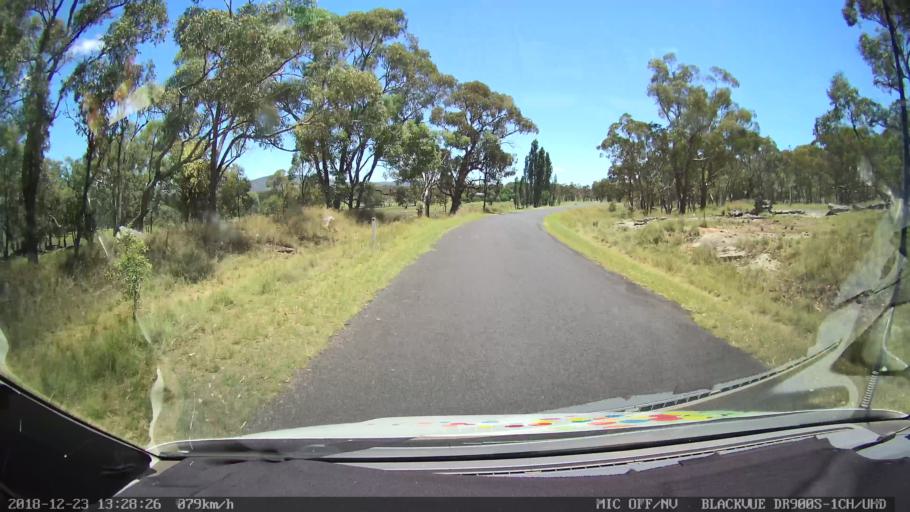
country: AU
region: New South Wales
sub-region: Armidale Dumaresq
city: Armidale
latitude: -30.4668
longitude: 151.3489
